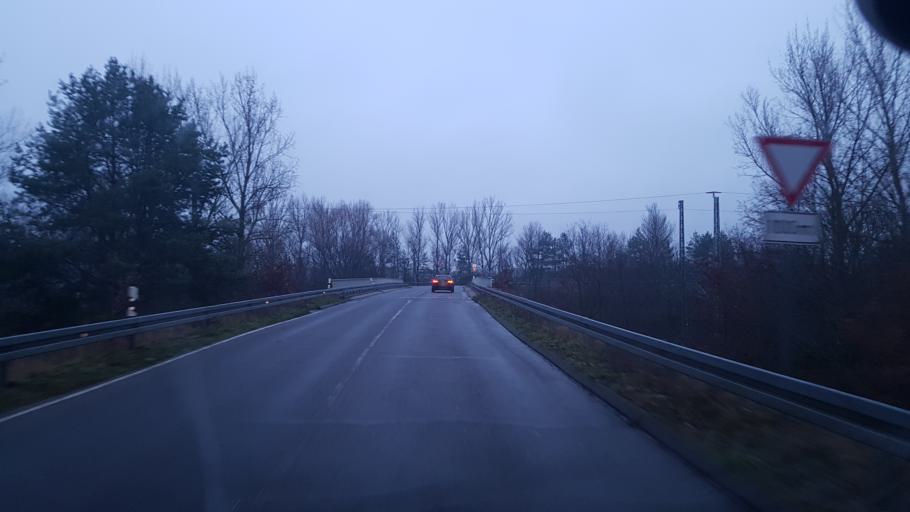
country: DE
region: Brandenburg
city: Ludwigsfelde
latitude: 52.3182
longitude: 13.2009
